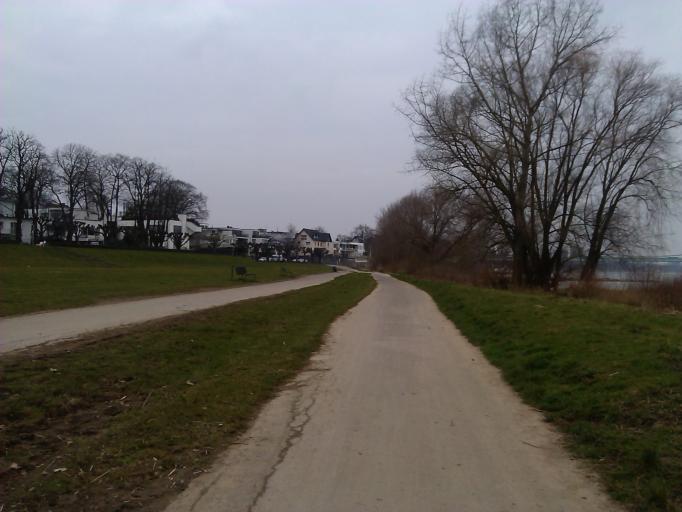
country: DE
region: North Rhine-Westphalia
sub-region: Regierungsbezirk Koln
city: Poll
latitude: 50.8930
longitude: 7.0021
